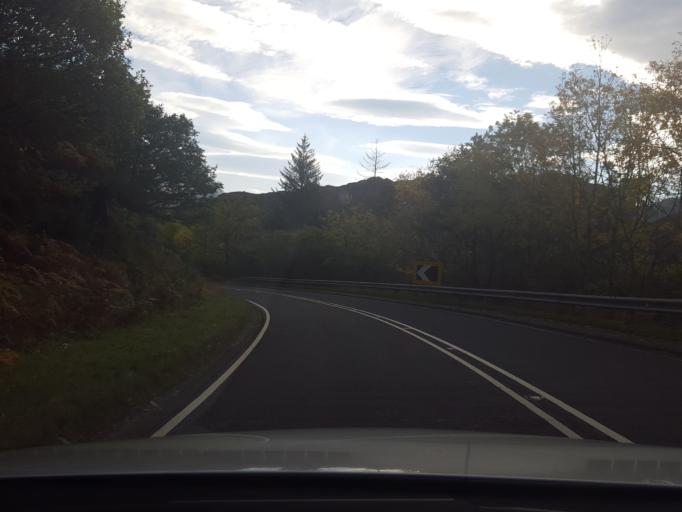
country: GB
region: Scotland
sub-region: Highland
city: Fort William
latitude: 57.2150
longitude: -5.4232
